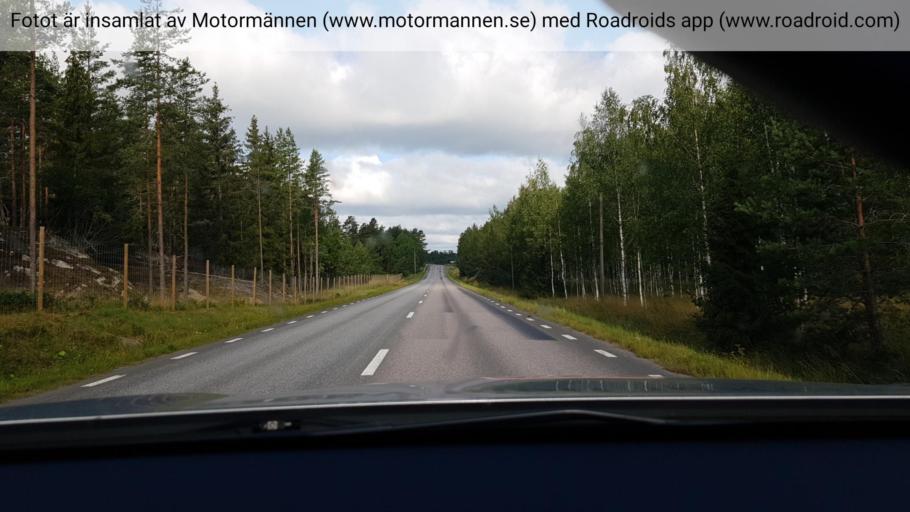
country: SE
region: Stockholm
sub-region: Norrtalje Kommun
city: Nykvarn
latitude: 59.8597
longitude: 18.0881
